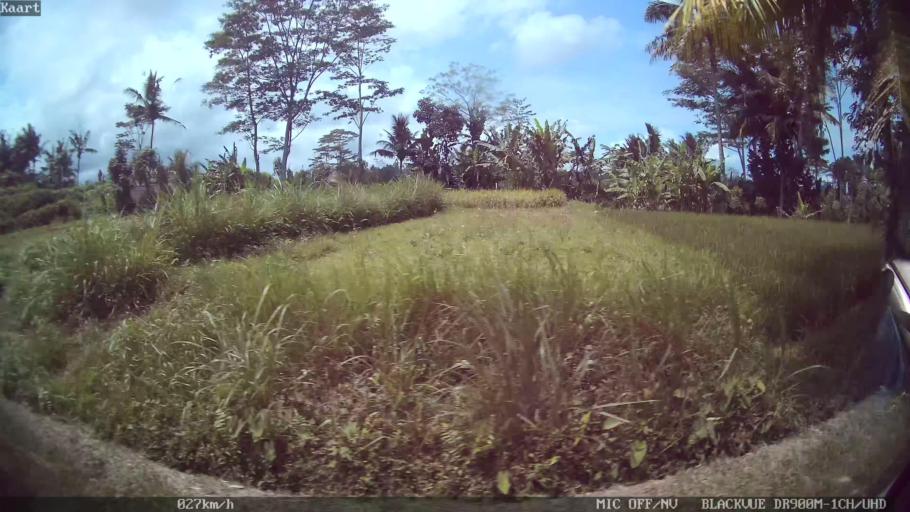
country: ID
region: Bali
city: Banjar Kelodan
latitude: -8.4899
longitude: 115.3686
